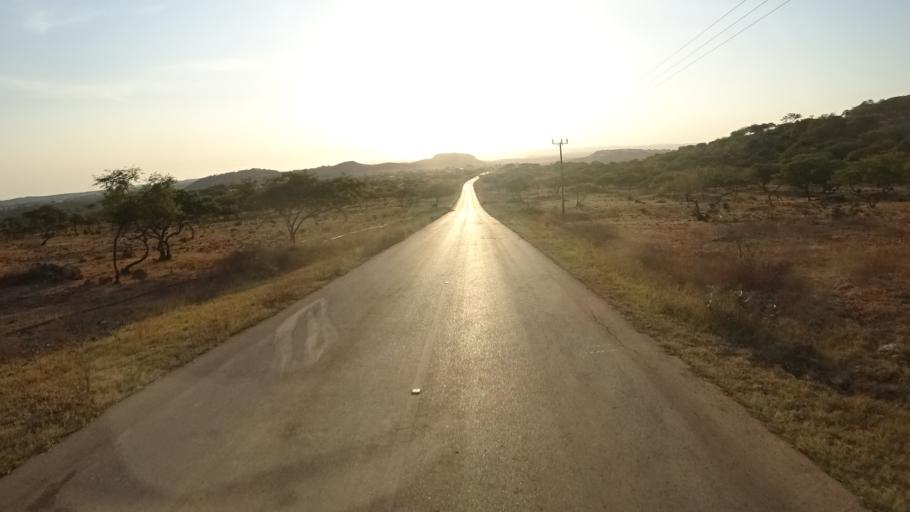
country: OM
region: Zufar
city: Salalah
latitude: 17.1486
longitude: 54.5974
